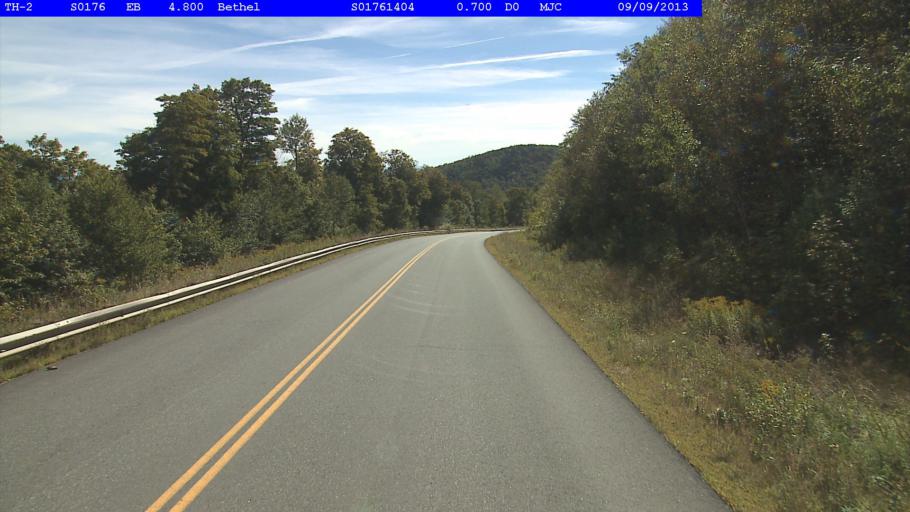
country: US
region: Vermont
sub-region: Orange County
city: Randolph
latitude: 43.8510
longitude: -72.7373
